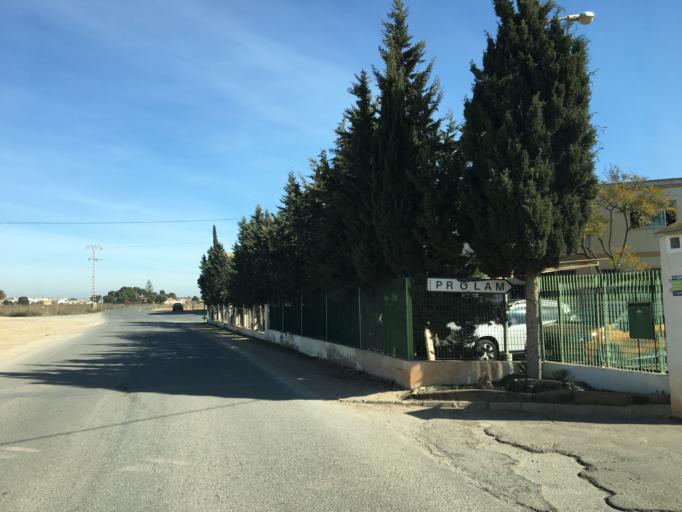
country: ES
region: Murcia
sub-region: Murcia
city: Cartagena
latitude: 37.6371
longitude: -1.0176
